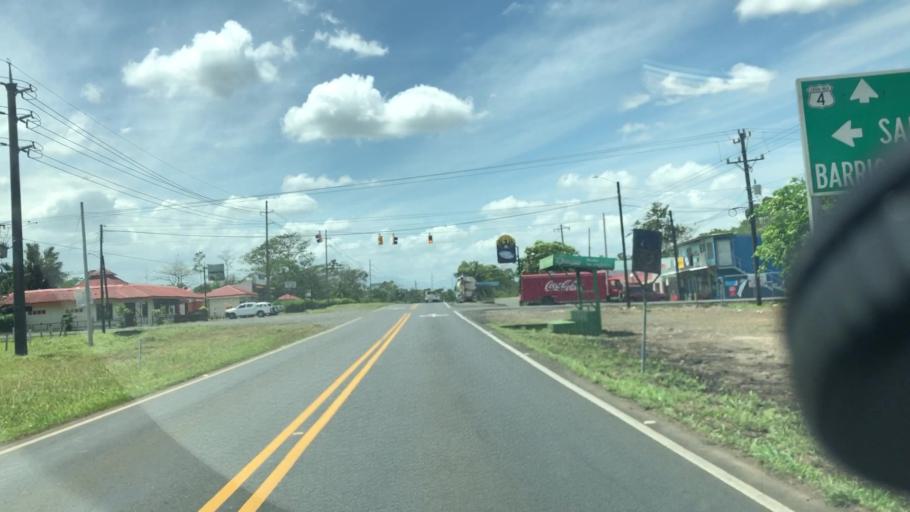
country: CR
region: Alajuela
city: Pital
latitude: 10.4567
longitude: -84.4066
